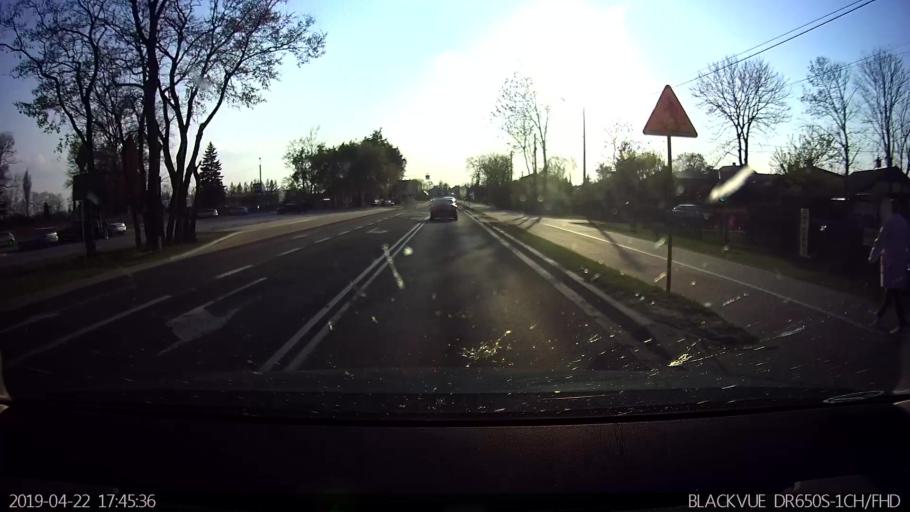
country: PL
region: Masovian Voivodeship
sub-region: Powiat wegrowski
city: Wegrow
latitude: 52.3999
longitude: 22.0341
